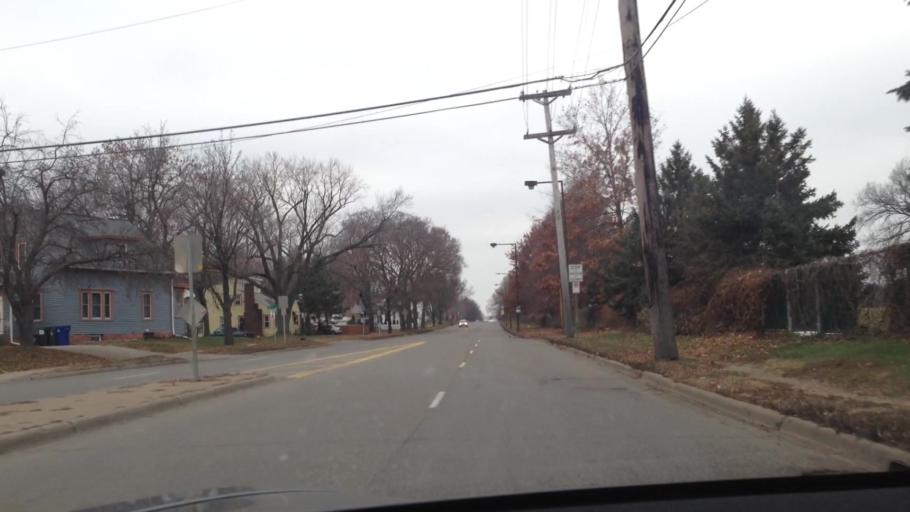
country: US
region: Minnesota
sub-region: Ramsey County
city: Falcon Heights
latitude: 44.9550
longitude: -93.1925
